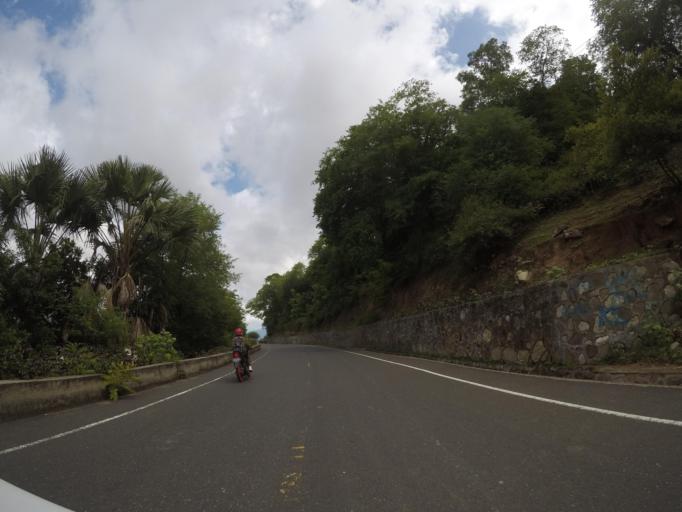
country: TL
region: Liquica
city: Maubara
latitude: -8.7432
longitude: 125.1234
